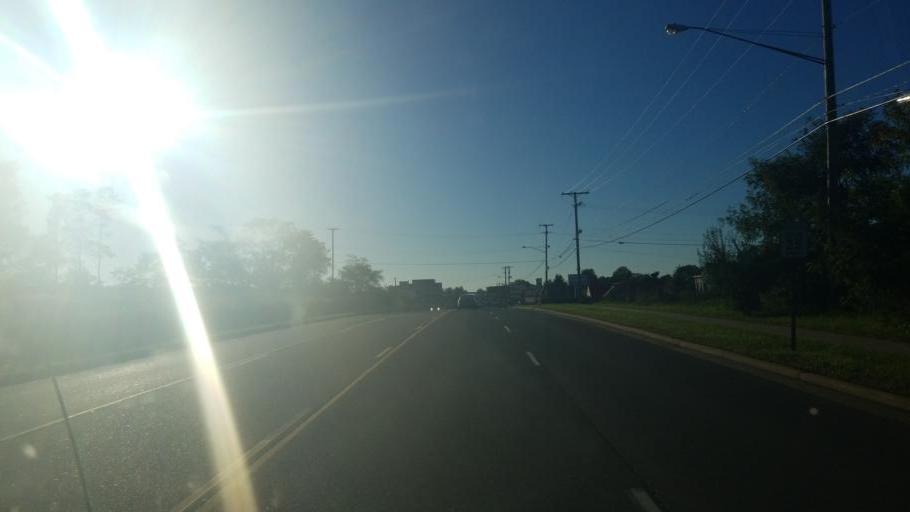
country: US
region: Ohio
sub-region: Columbiana County
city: Salem
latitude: 40.9010
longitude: -80.8233
